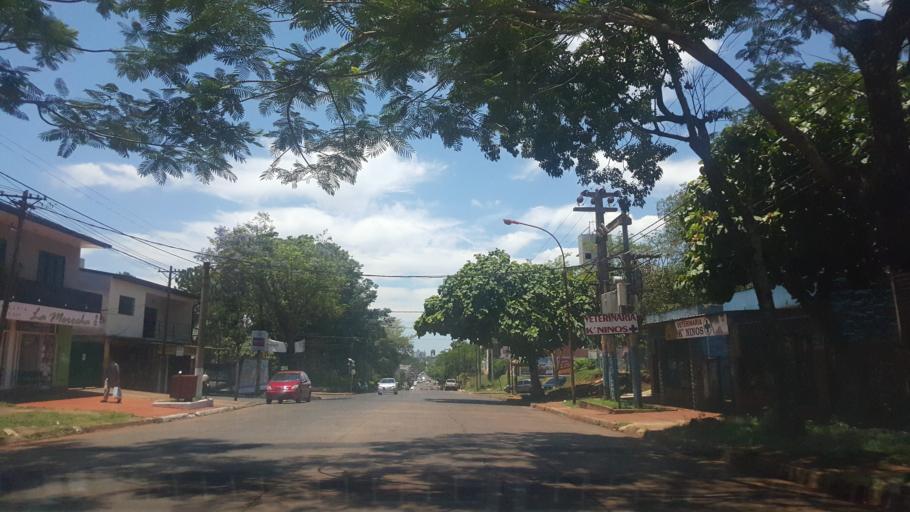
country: AR
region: Misiones
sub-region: Departamento de Capital
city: Posadas
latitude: -27.3684
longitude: -55.9212
